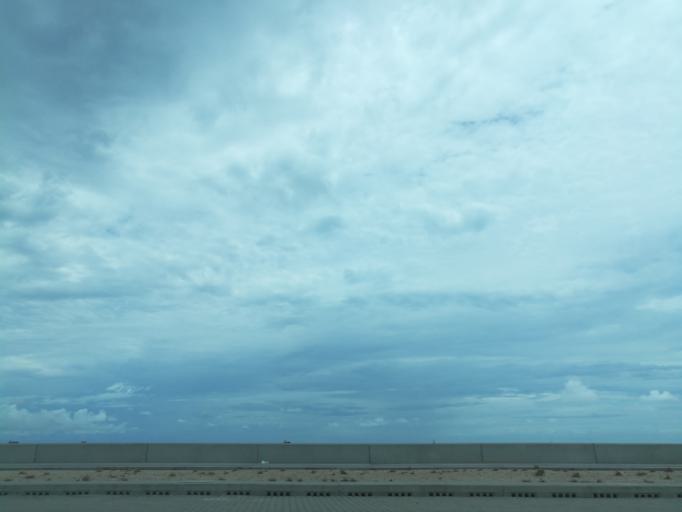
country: NG
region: Lagos
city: Ikoyi
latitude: 6.4041
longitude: 3.4155
